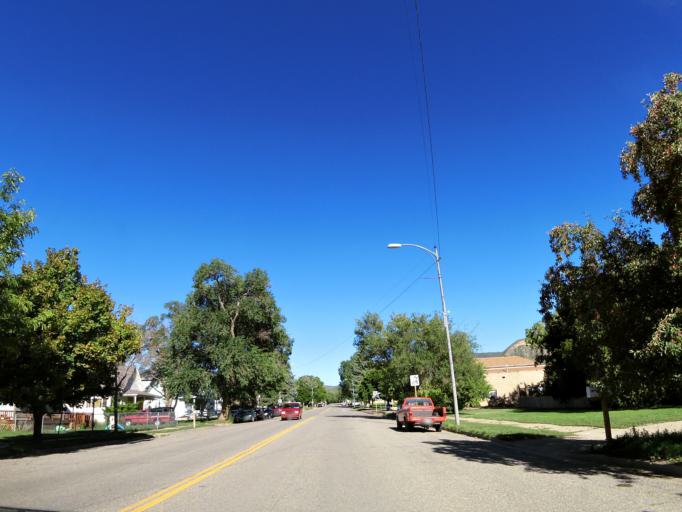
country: US
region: Colorado
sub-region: Montezuma County
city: Mancos
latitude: 37.3450
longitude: -108.2943
